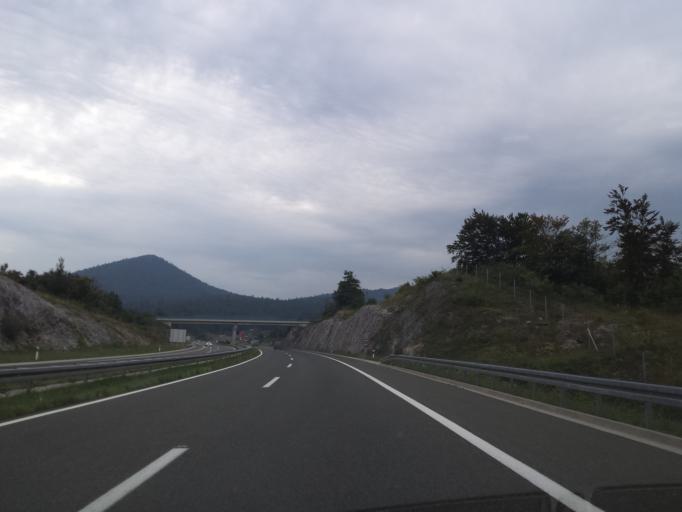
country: HR
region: Karlovacka
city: Ostarije
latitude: 45.1237
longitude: 15.2432
